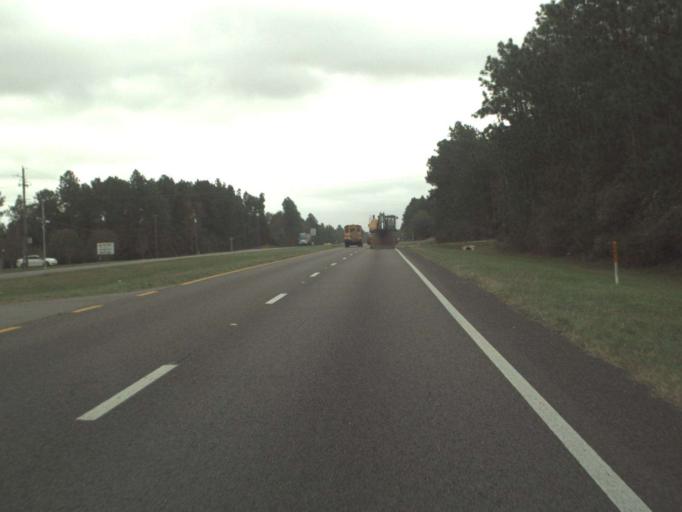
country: US
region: Florida
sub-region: Escambia County
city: Molino
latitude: 30.6749
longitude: -87.3511
